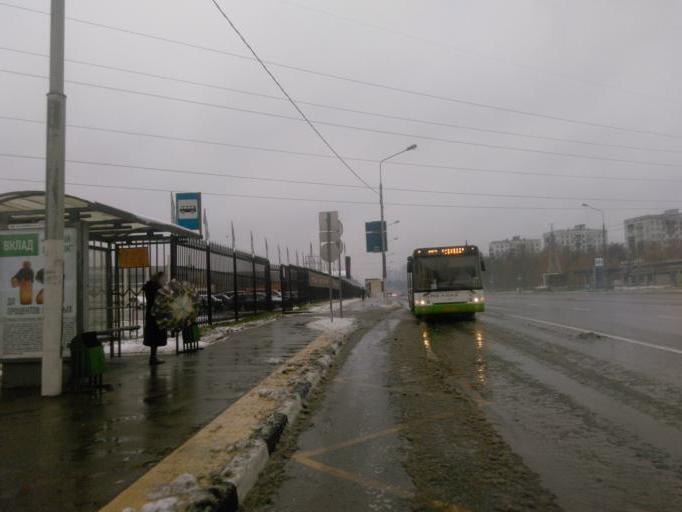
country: RU
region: Moscow
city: Kotlovka
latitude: 55.6429
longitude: 37.5880
